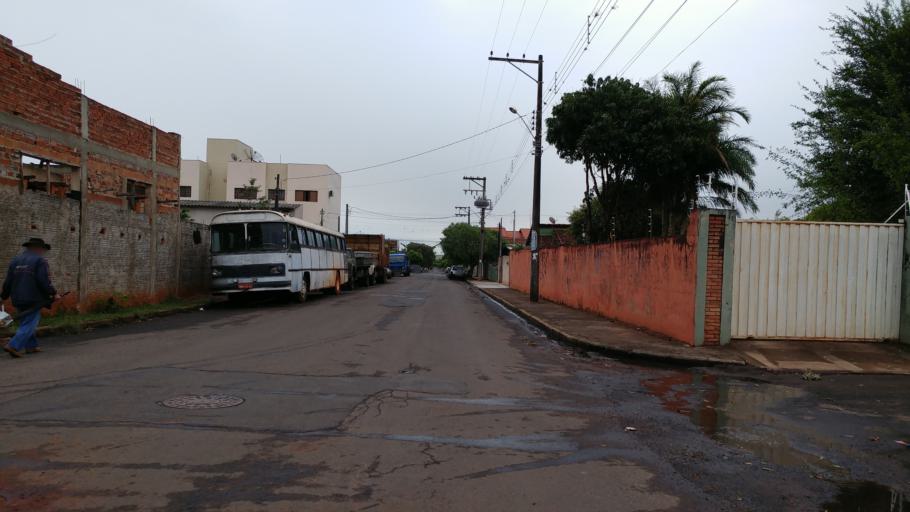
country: BR
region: Sao Paulo
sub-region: Paraguacu Paulista
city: Paraguacu Paulista
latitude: -22.4196
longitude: -50.5841
